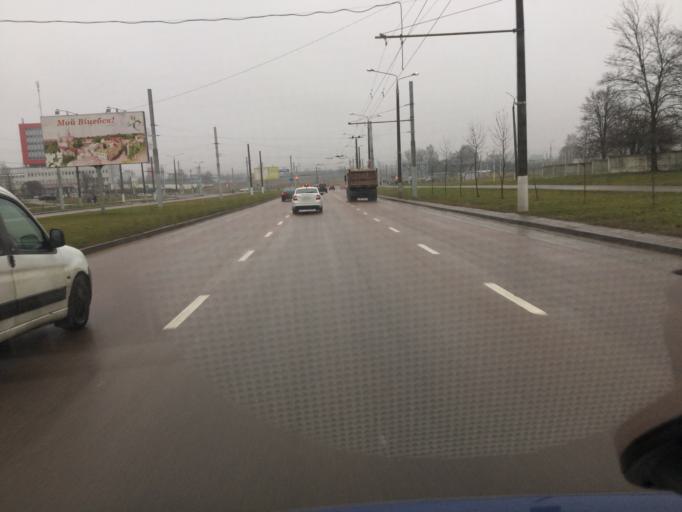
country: BY
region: Vitebsk
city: Vitebsk
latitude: 55.1589
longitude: 30.2303
